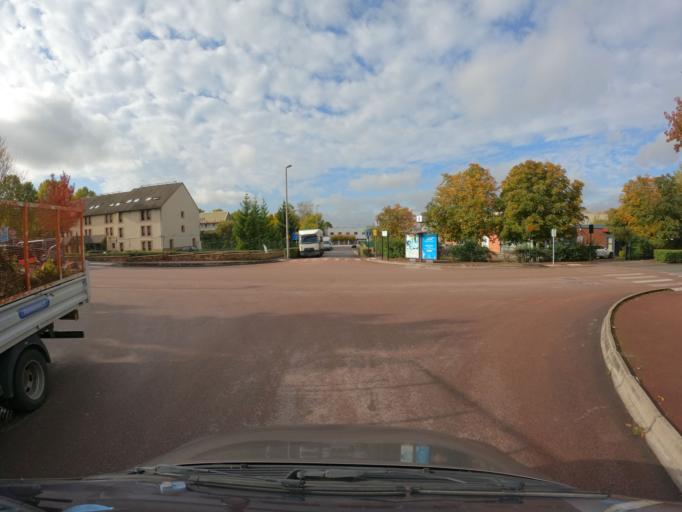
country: FR
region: Ile-de-France
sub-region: Departement de Seine-et-Marne
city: Chelles
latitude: 48.8897
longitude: 2.5942
